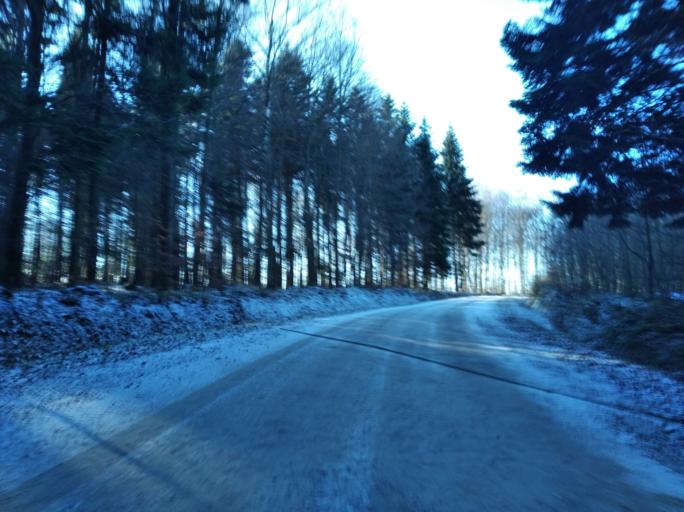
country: PL
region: Subcarpathian Voivodeship
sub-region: Powiat strzyzowski
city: Czudec
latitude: 49.9717
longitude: 21.7901
